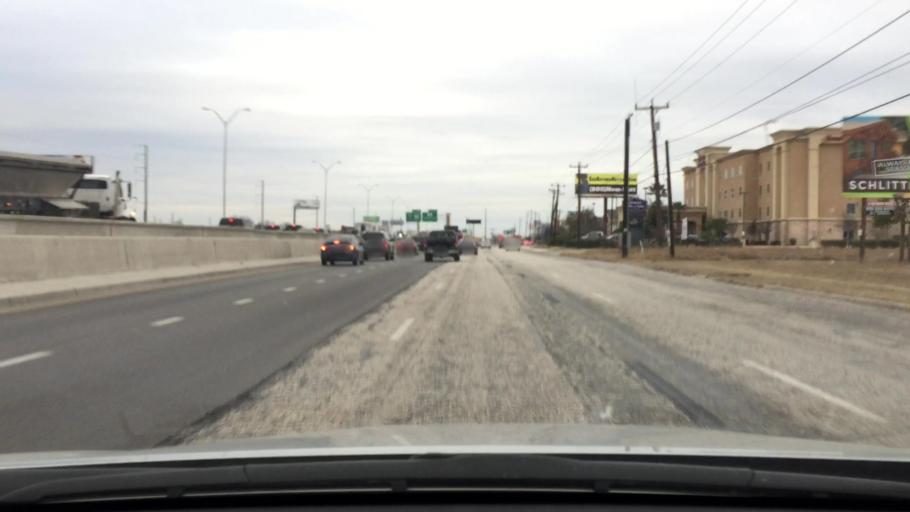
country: US
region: Texas
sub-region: Bexar County
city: Kirby
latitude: 29.4903
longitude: -98.4015
